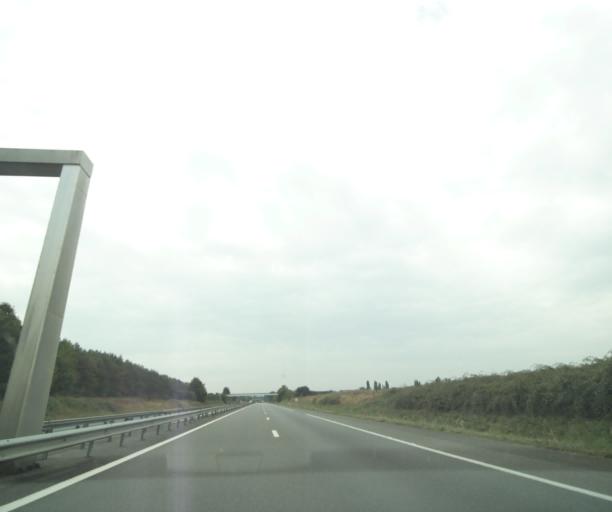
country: FR
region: Pays de la Loire
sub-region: Departement de la Vendee
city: Bouffere
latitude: 46.9584
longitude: -1.3569
